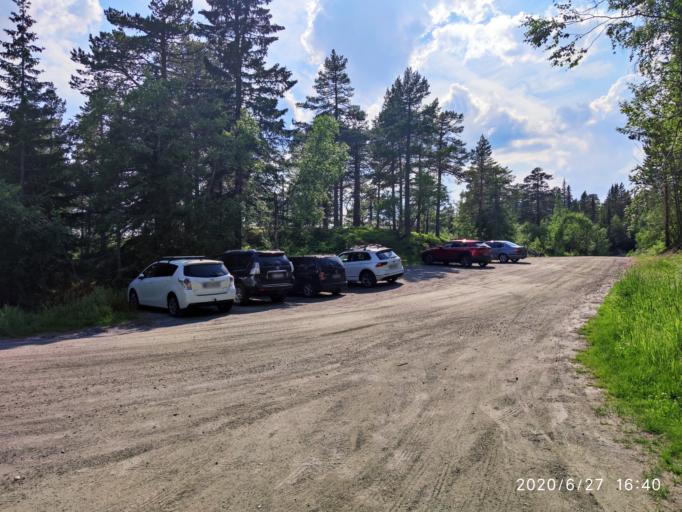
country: NO
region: Buskerud
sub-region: Kongsberg
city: Kongsberg
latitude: 59.6656
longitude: 9.5790
